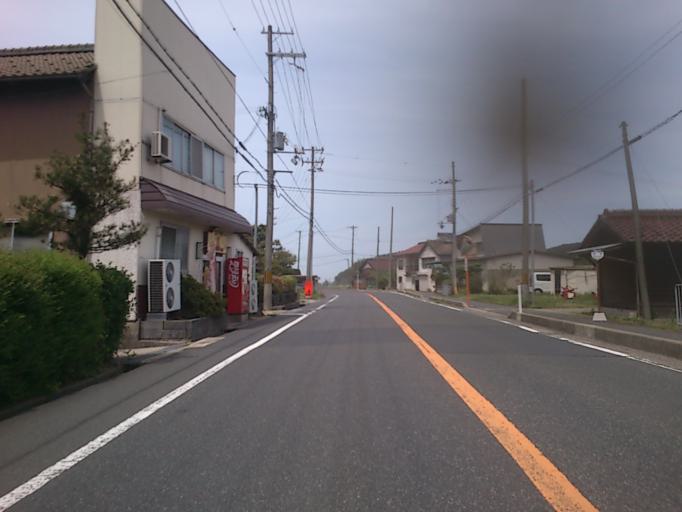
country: JP
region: Kyoto
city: Miyazu
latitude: 35.7195
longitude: 135.1042
